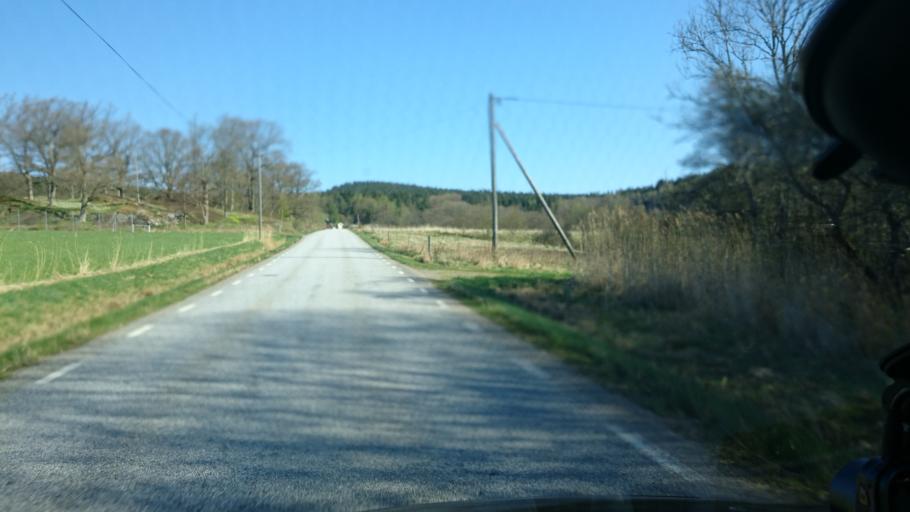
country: SE
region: Vaestra Goetaland
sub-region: Munkedals Kommun
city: Munkedal
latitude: 58.3945
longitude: 11.6532
